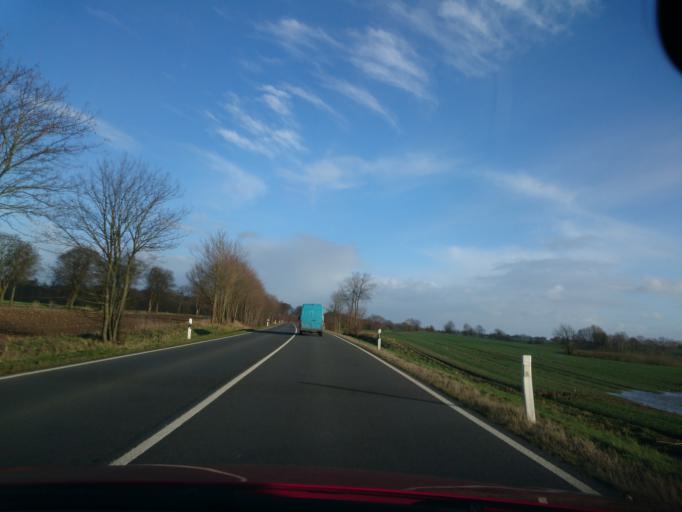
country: DE
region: Mecklenburg-Vorpommern
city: Mesekenhagen
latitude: 54.2071
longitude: 13.2519
